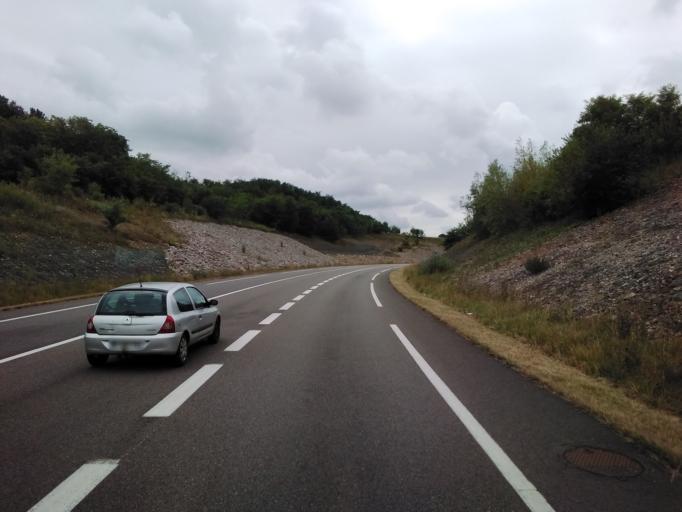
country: FR
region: Franche-Comte
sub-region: Departement du Jura
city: Montmorot
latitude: 46.6744
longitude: 5.5111
